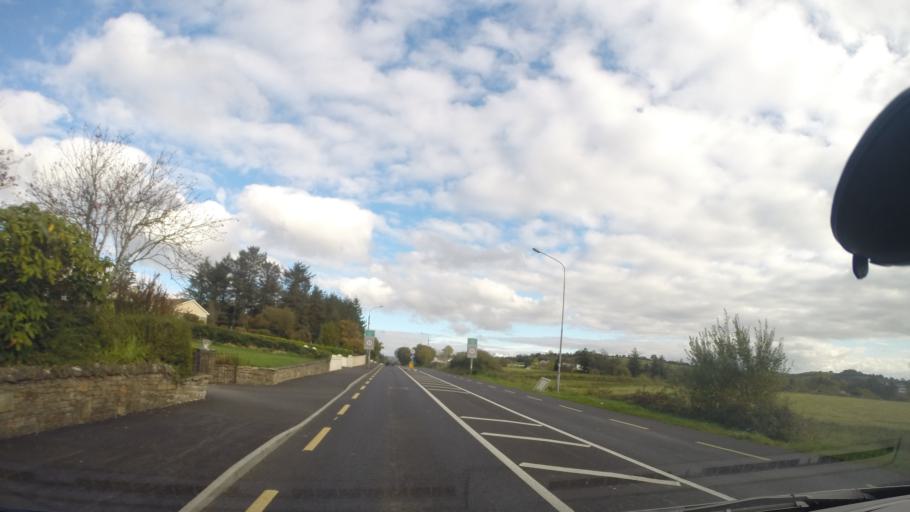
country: IE
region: Ulster
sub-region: County Donegal
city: Donegal
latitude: 54.6552
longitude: -8.1276
